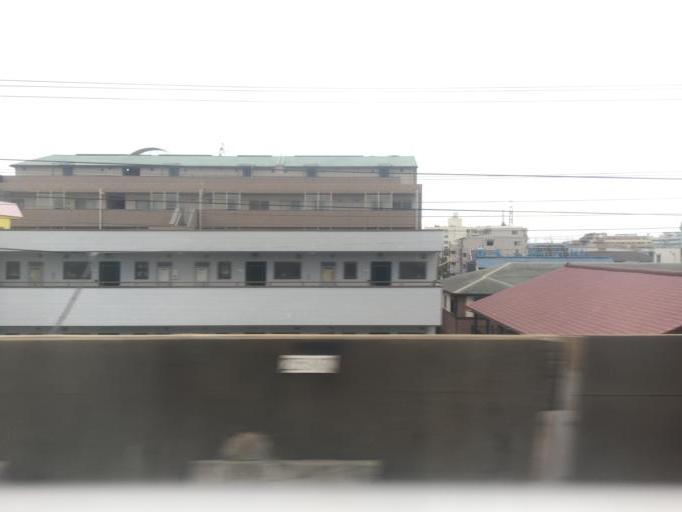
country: JP
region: Tokyo
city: Urayasu
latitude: 35.6786
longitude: 139.9095
